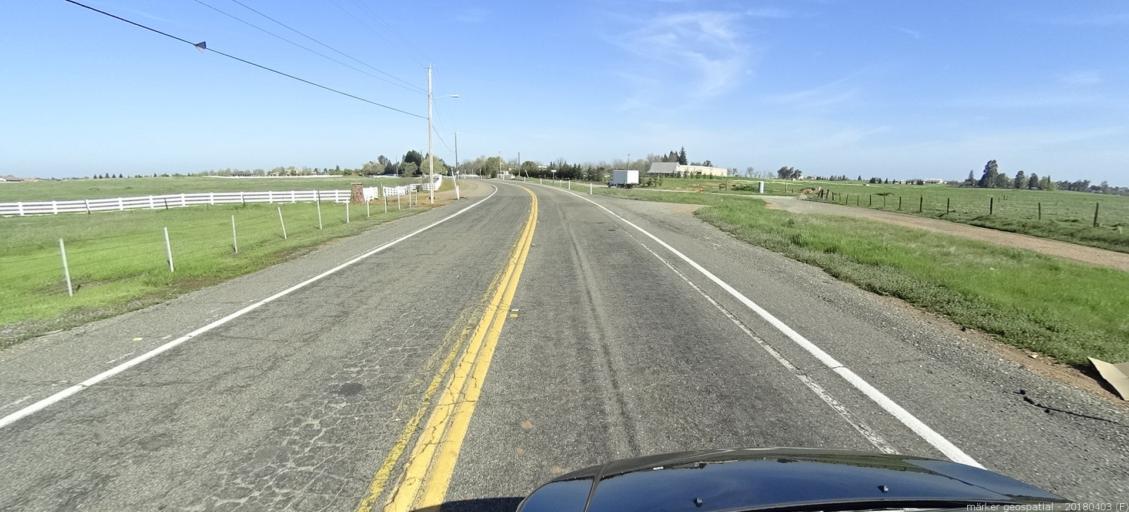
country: US
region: California
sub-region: Sacramento County
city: Clay
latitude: 38.4129
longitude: -121.1757
